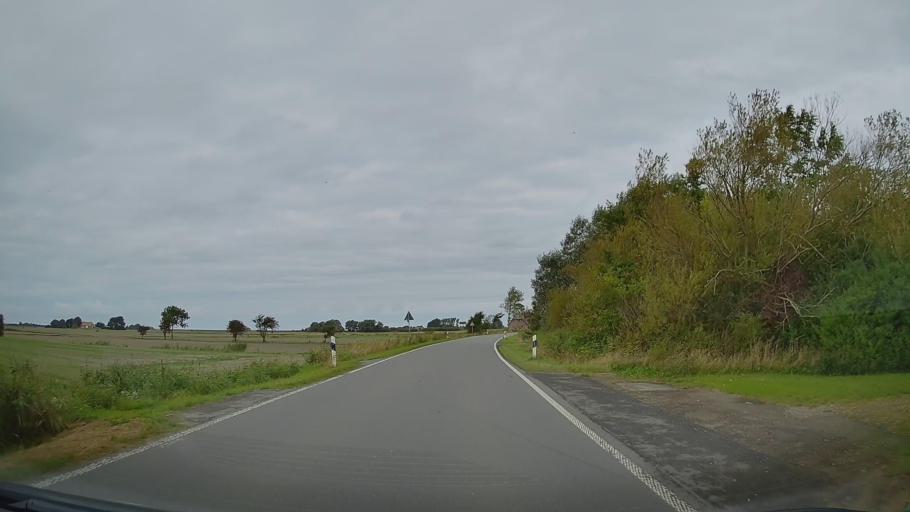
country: DE
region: Schleswig-Holstein
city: Klanxbull
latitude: 54.8768
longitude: 8.6821
